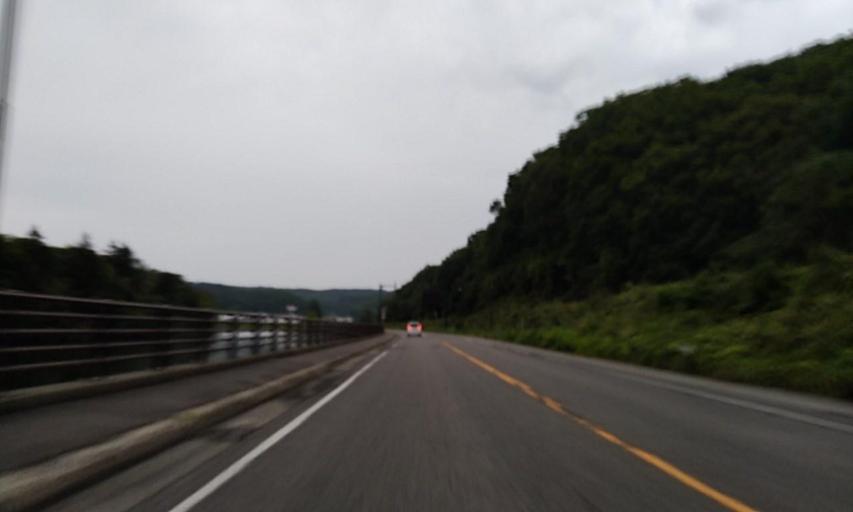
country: JP
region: Hokkaido
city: Abashiri
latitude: 44.0065
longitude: 144.2316
